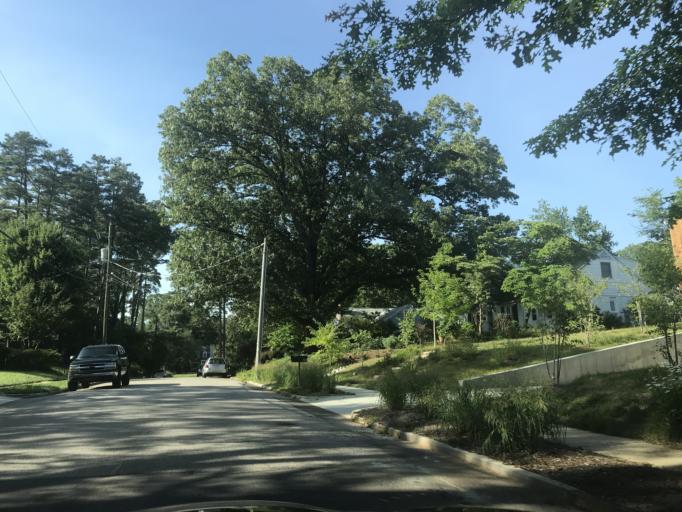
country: US
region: North Carolina
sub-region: Wake County
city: West Raleigh
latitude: 35.7951
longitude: -78.6774
